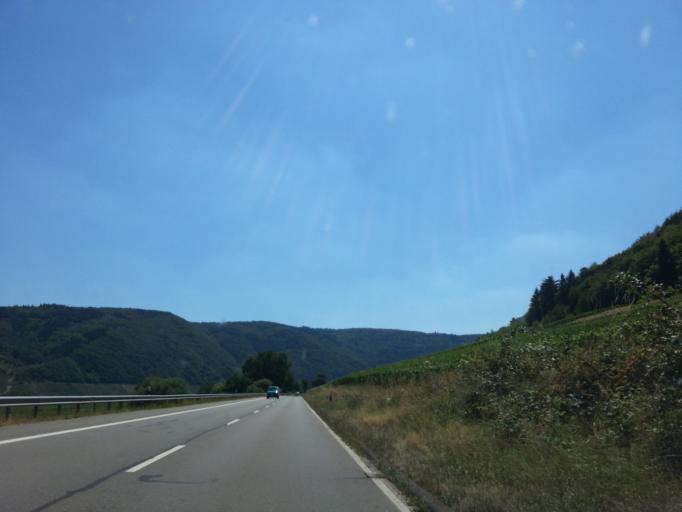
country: DE
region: Rheinland-Pfalz
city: Detzem
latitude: 49.8089
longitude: 6.8431
